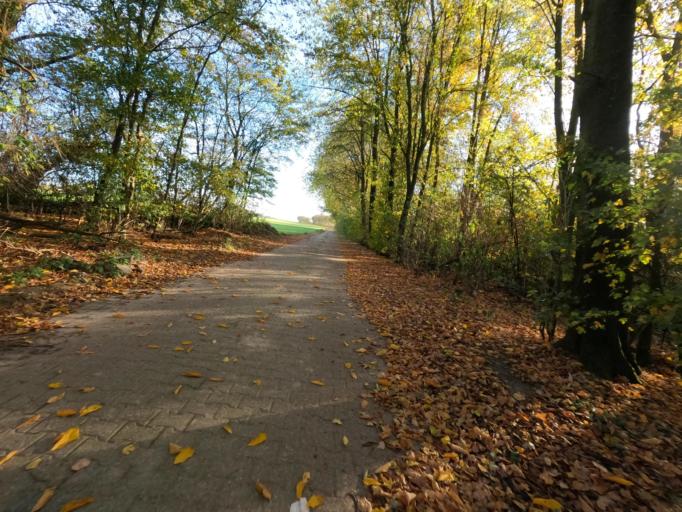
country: DE
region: North Rhine-Westphalia
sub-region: Regierungsbezirk Koln
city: Titz
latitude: 51.0375
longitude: 6.4011
